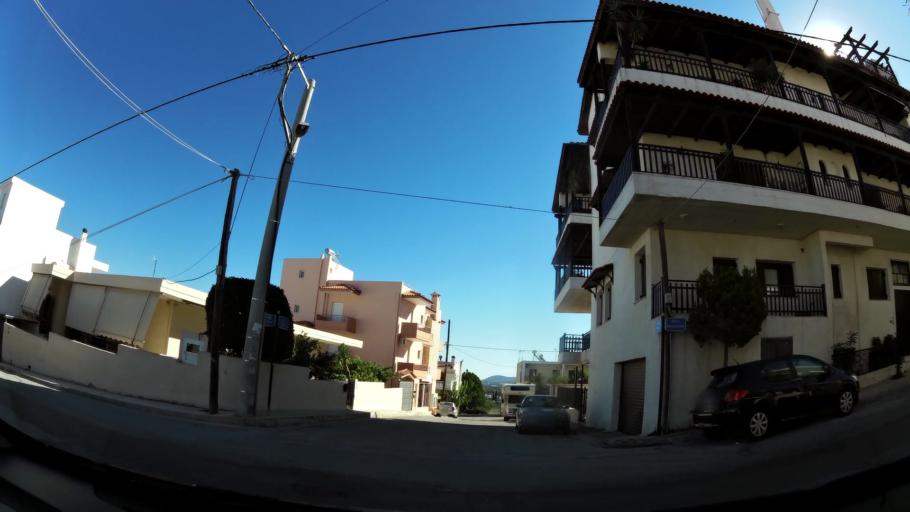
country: GR
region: Attica
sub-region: Nomarchia Anatolikis Attikis
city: Koropi
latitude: 37.9014
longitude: 23.8818
